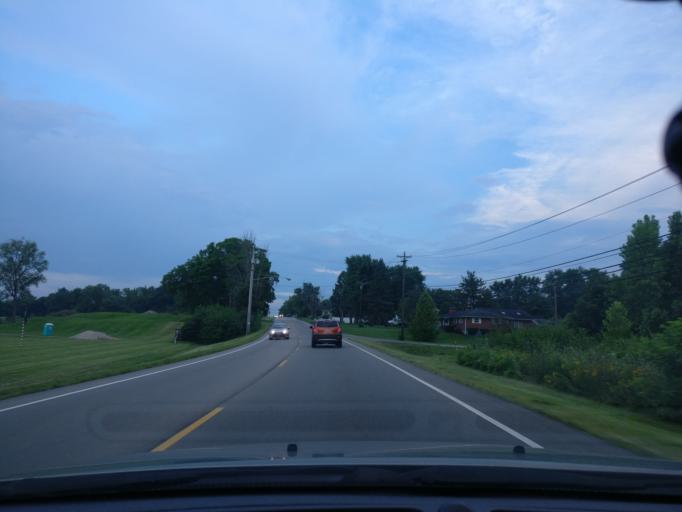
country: US
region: Ohio
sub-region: Warren County
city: Franklin
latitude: 39.5502
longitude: -84.2980
